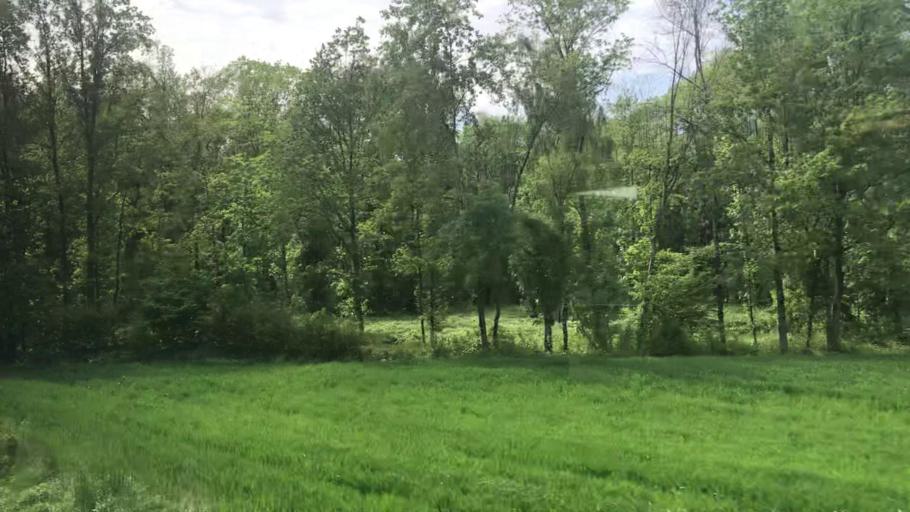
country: PL
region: Lower Silesian Voivodeship
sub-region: Powiat wroclawski
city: Katy Wroclawskie
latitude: 51.0034
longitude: 16.6928
